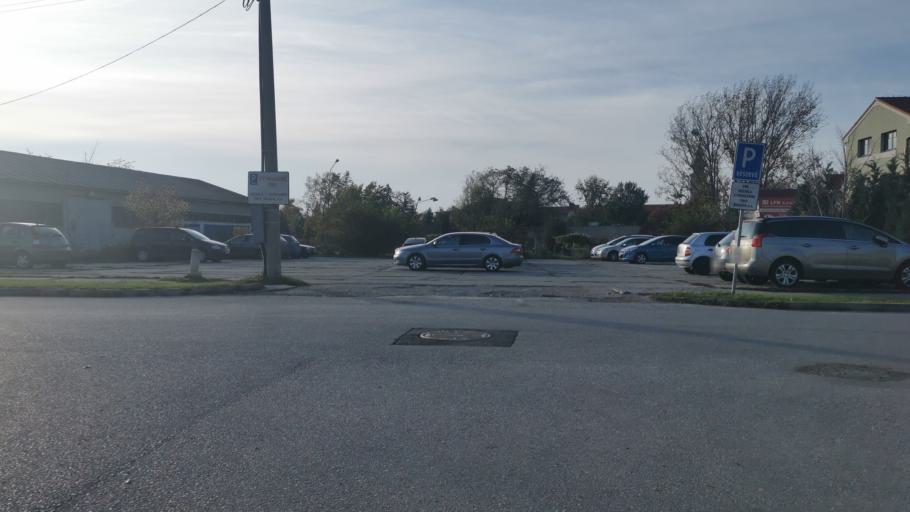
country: SK
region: Trnavsky
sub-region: Okres Skalica
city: Skalica
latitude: 48.8436
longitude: 17.2314
